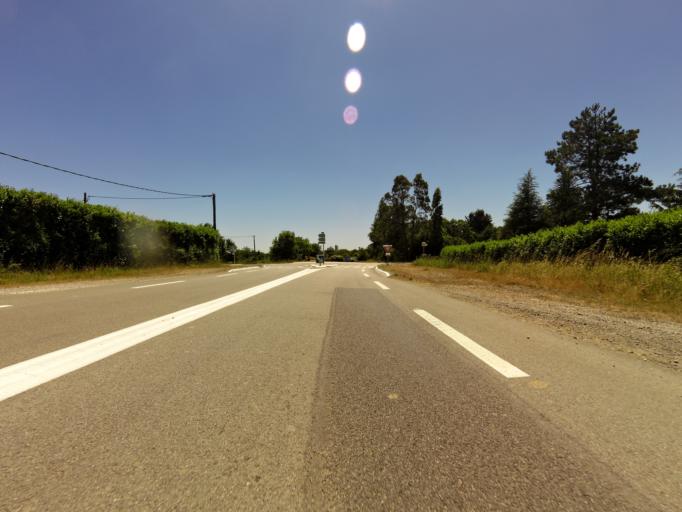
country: FR
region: Brittany
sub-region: Departement du Morbihan
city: Ferel
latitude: 47.5180
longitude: -2.3716
